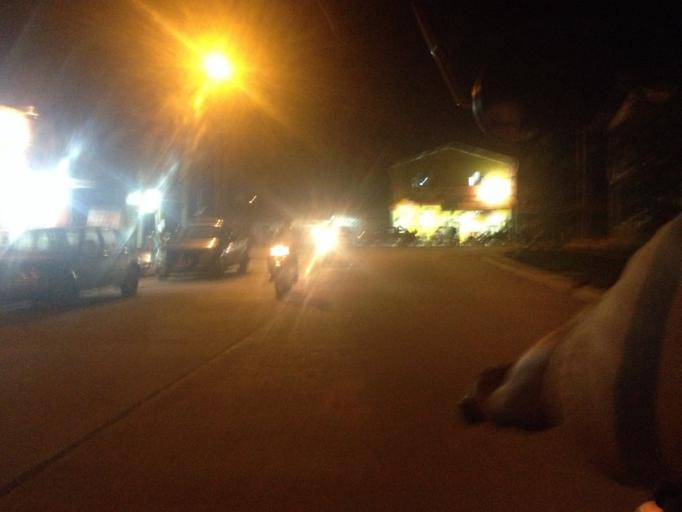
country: PE
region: Ucayali
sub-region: Provincia de Coronel Portillo
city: Pucallpa
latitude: -8.4001
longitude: -74.5674
